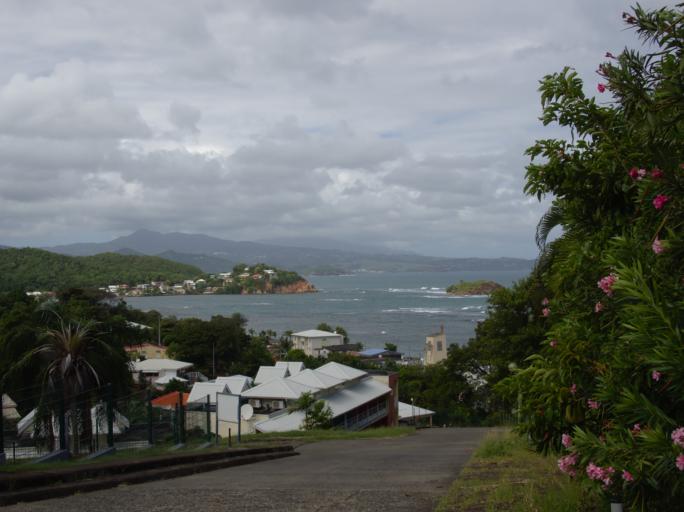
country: MQ
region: Martinique
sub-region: Martinique
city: Sainte-Marie
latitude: 14.7776
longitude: -61.0115
